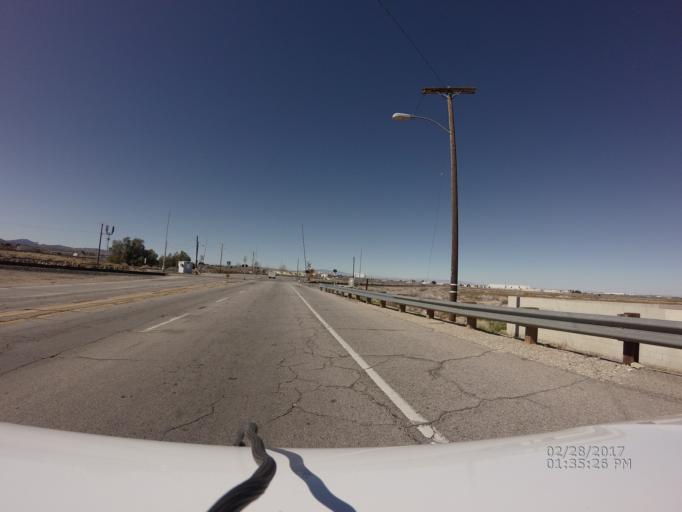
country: US
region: California
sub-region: Los Angeles County
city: Palmdale
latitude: 34.5924
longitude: -118.1190
